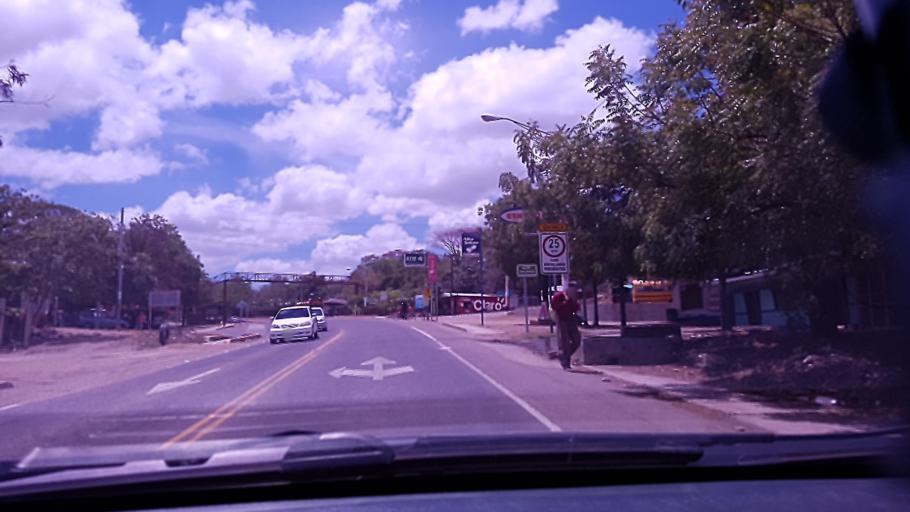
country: NI
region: Esteli
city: Condega
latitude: 13.3617
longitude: -86.4008
